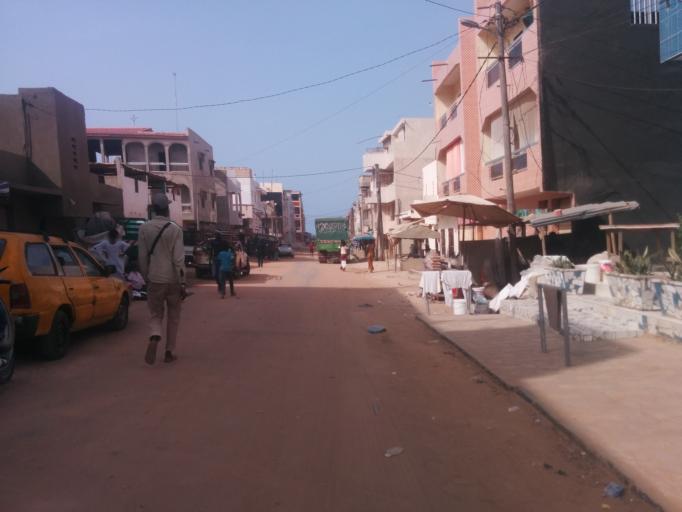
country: SN
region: Dakar
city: Pikine
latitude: 14.7645
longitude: -17.4395
